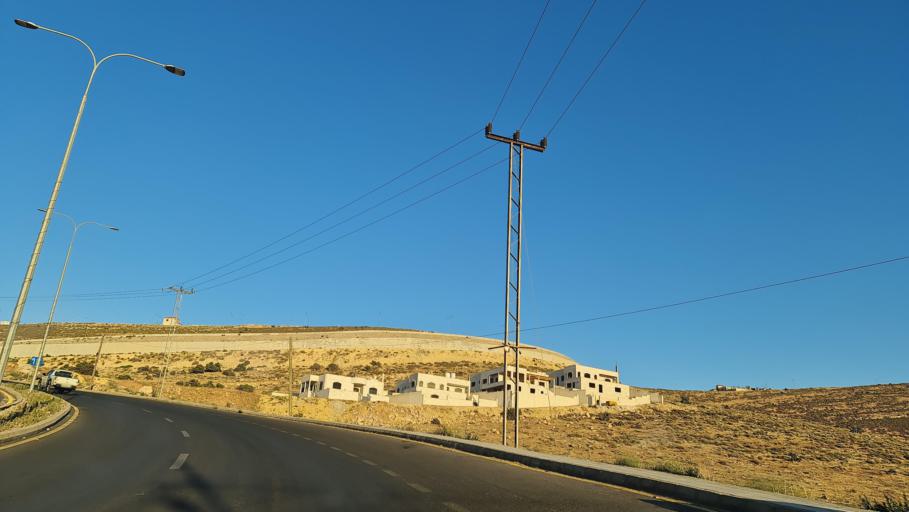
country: JO
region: Amman
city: Al Jubayhah
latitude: 32.0938
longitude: 35.9583
